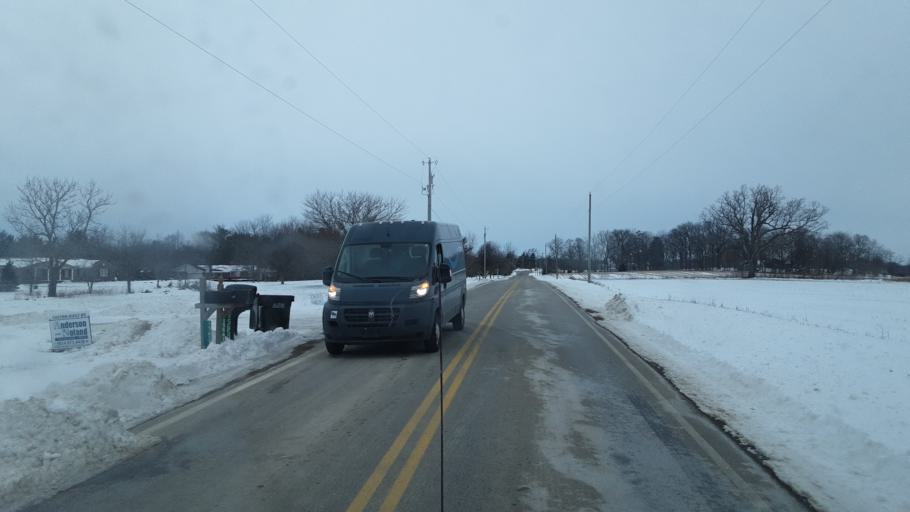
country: US
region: Ohio
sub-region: Madison County
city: Plain City
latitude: 40.1419
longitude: -83.3304
